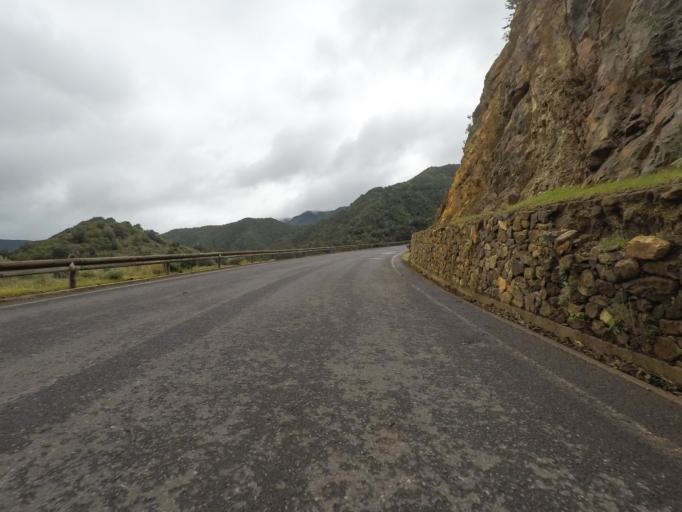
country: ES
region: Canary Islands
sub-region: Provincia de Santa Cruz de Tenerife
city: Vallehermosa
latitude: 28.1613
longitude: -17.2851
